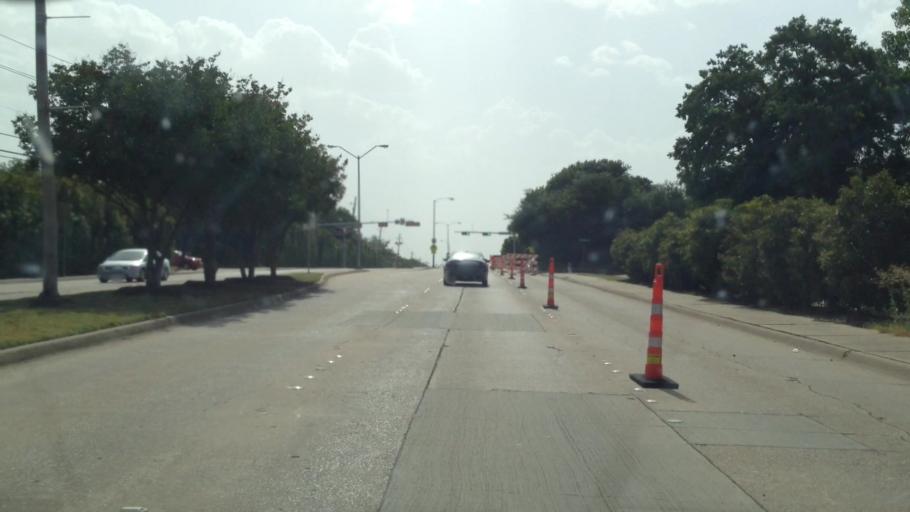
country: US
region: Texas
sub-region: Collin County
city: Plano
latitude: 33.0267
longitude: -96.7466
